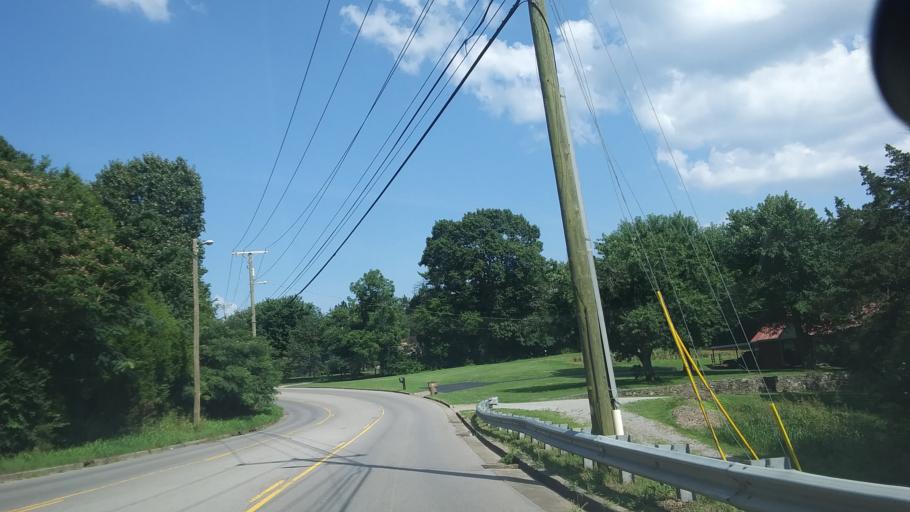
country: US
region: Tennessee
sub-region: Rutherford County
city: La Vergne
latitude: 36.0966
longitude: -86.6448
